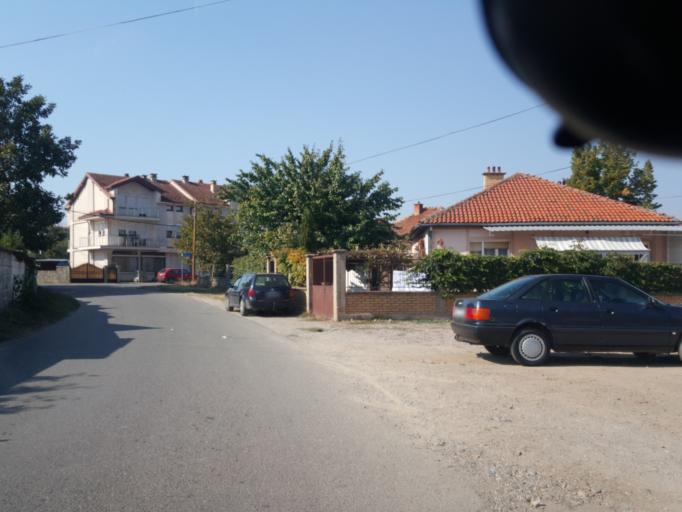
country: XK
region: Gjakova
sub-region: Komuna e Gjakoves
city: Gjakove
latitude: 42.3907
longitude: 20.4309
